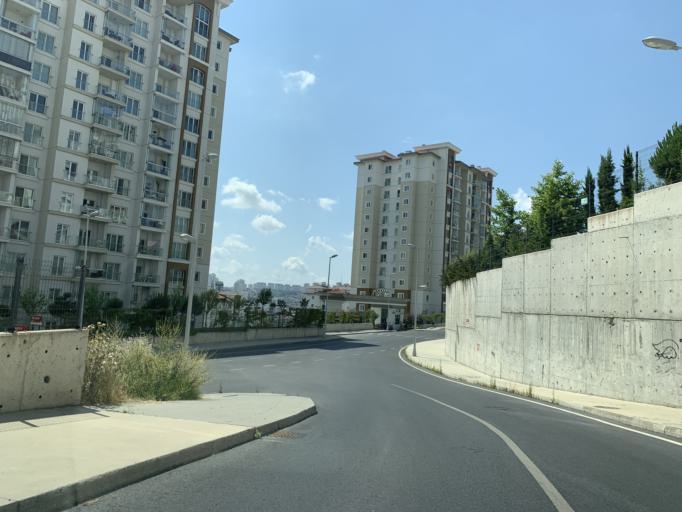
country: TR
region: Istanbul
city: Esenyurt
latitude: 41.0743
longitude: 28.6961
